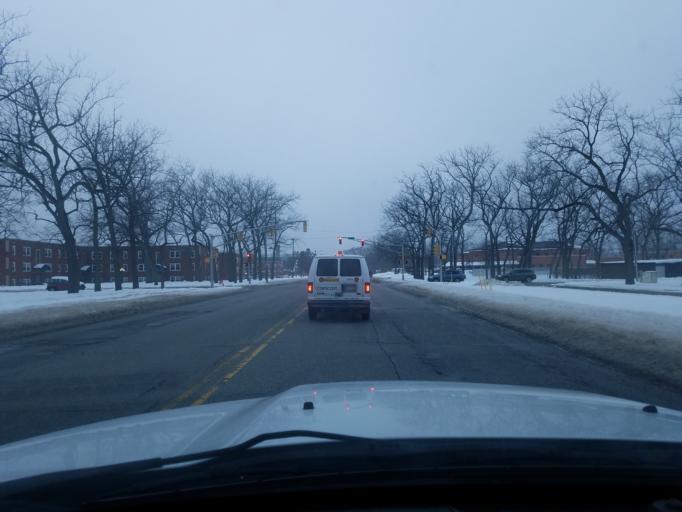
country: US
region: Indiana
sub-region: Saint Joseph County
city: Notre Dame
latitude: 41.6729
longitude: -86.2097
